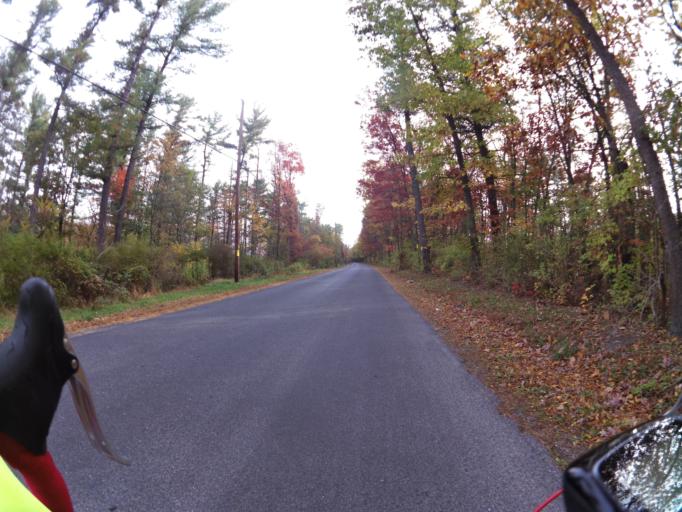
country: US
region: Pennsylvania
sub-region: Union County
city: New Columbia
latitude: 41.0418
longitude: -76.9179
